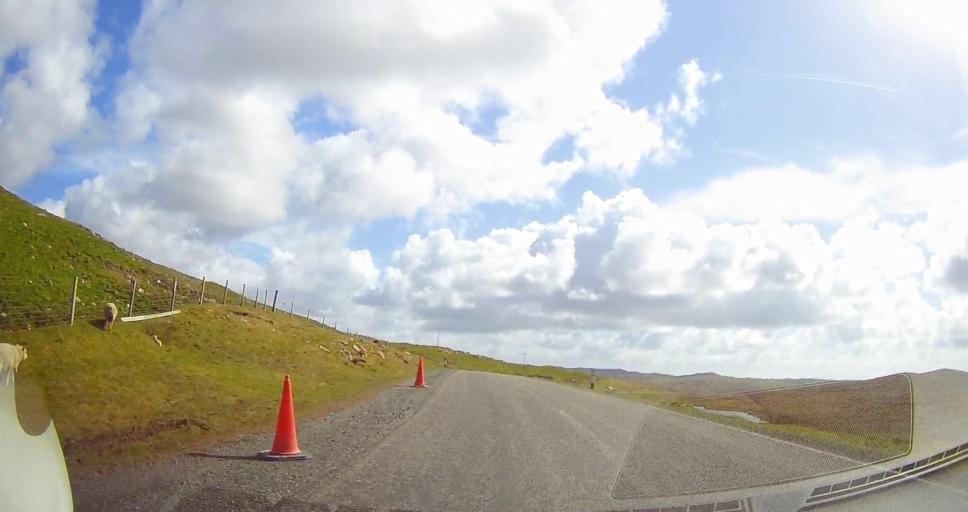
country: GB
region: Scotland
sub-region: Shetland Islands
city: Lerwick
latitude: 60.4856
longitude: -1.4027
